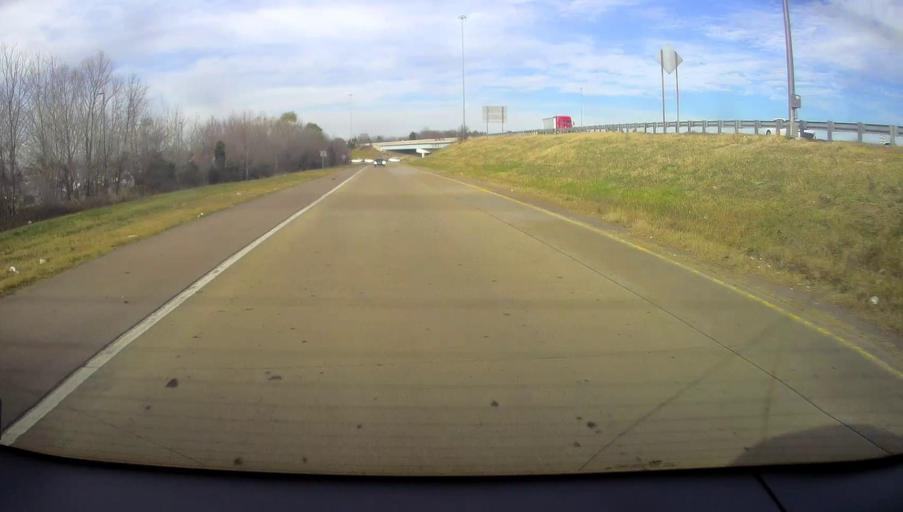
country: US
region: Tennessee
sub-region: Shelby County
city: Germantown
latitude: 35.0476
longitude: -89.8093
